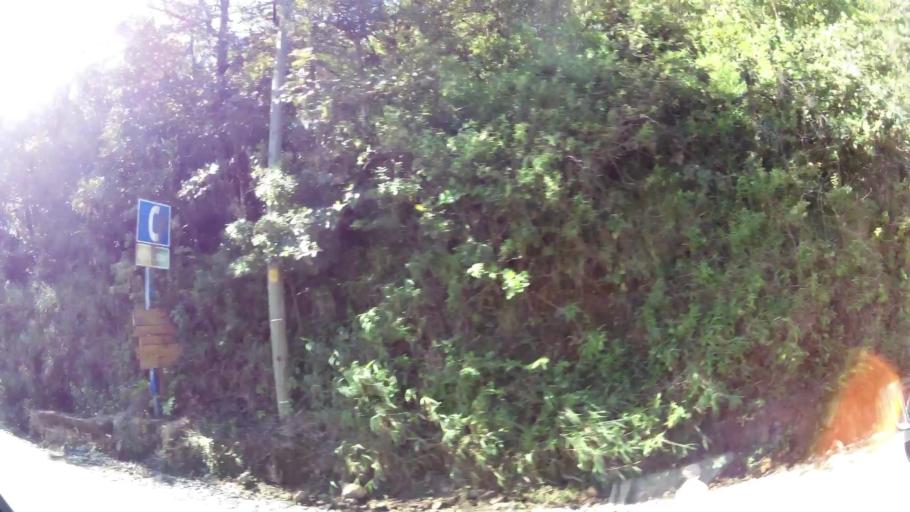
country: CR
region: Guanacaste
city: Juntas
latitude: 10.3294
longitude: -84.8453
